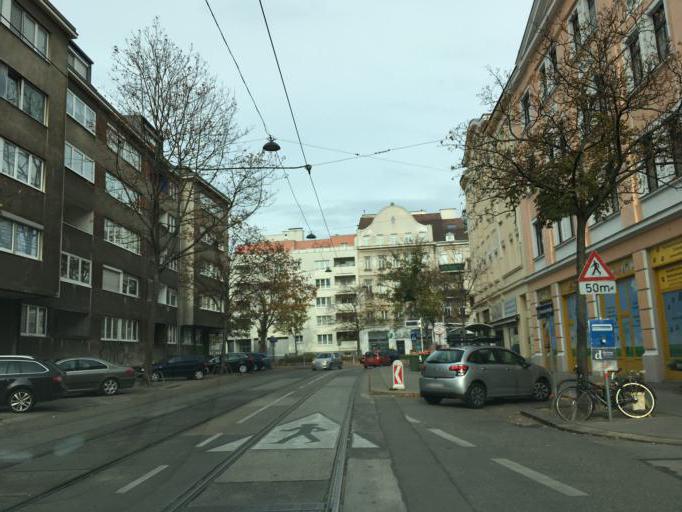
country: AT
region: Vienna
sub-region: Wien Stadt
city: Vienna
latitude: 48.2018
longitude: 16.3267
